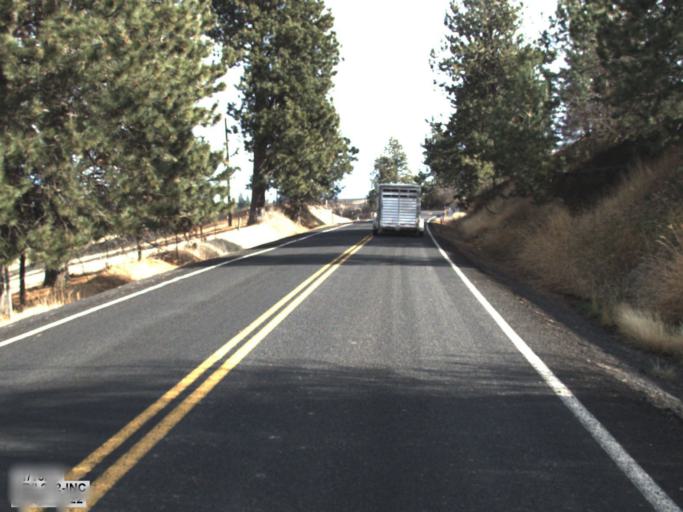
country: US
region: Washington
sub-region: Whitman County
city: Pullman
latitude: 46.9151
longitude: -117.0964
